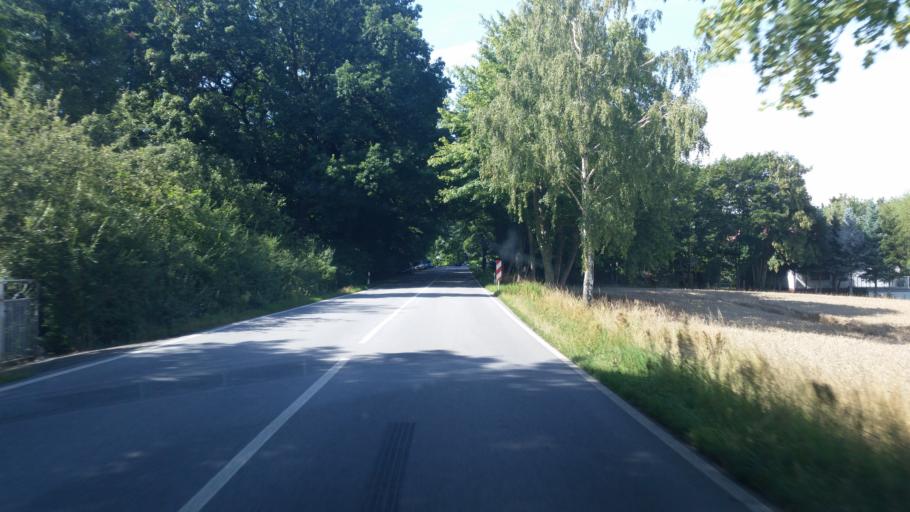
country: DE
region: Saxony
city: Kamenz
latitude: 51.2793
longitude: 14.0727
